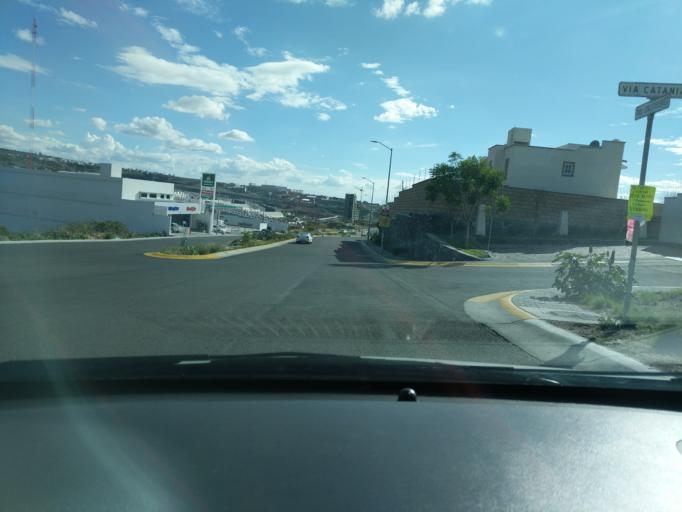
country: MX
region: Queretaro
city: La Canada
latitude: 20.5913
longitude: -100.3299
